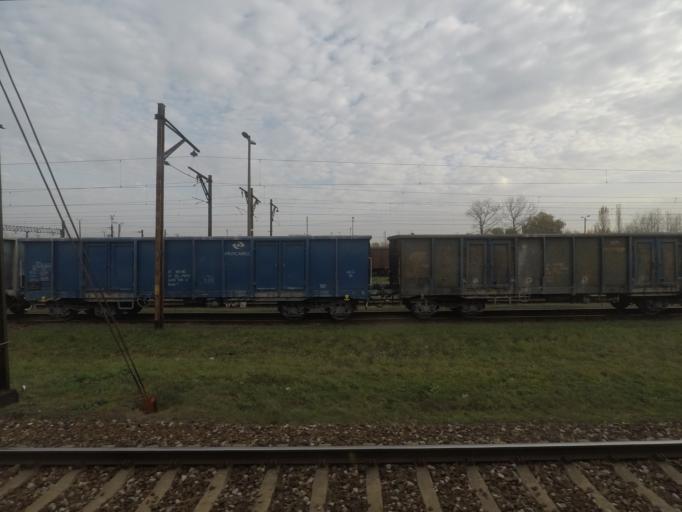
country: PL
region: Subcarpathian Voivodeship
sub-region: Powiat przemyski
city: Orly
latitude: 49.8373
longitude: 22.8411
